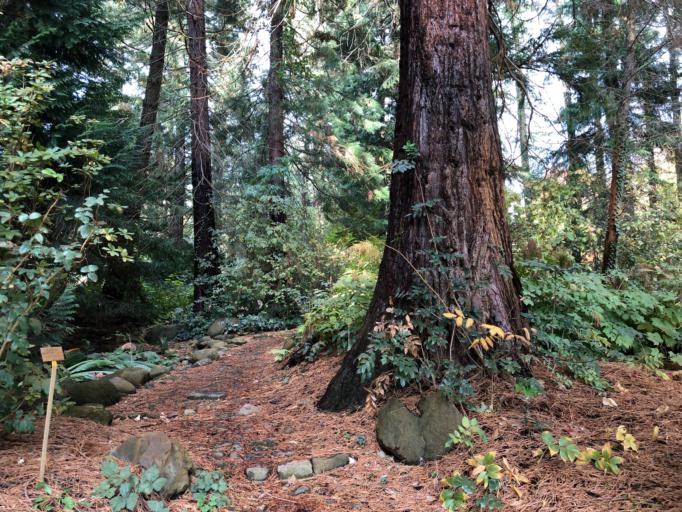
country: DE
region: Berlin
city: Lichterfelde
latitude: 52.4530
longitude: 13.3066
